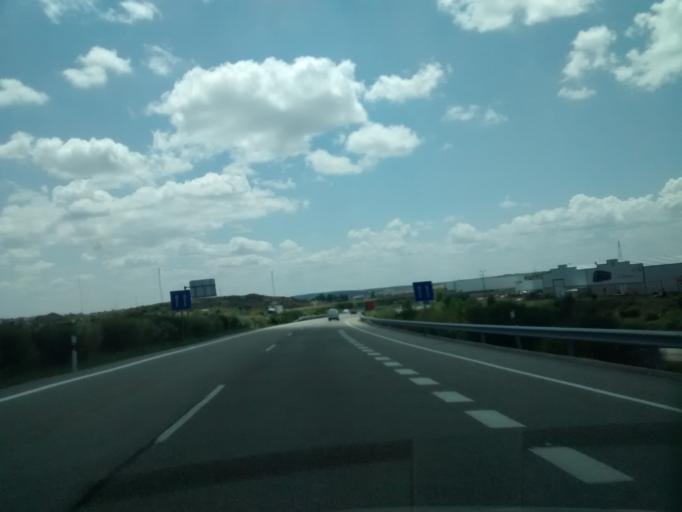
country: ES
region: Castille and Leon
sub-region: Provincia de Leon
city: Astorga
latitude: 42.4714
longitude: -6.0841
